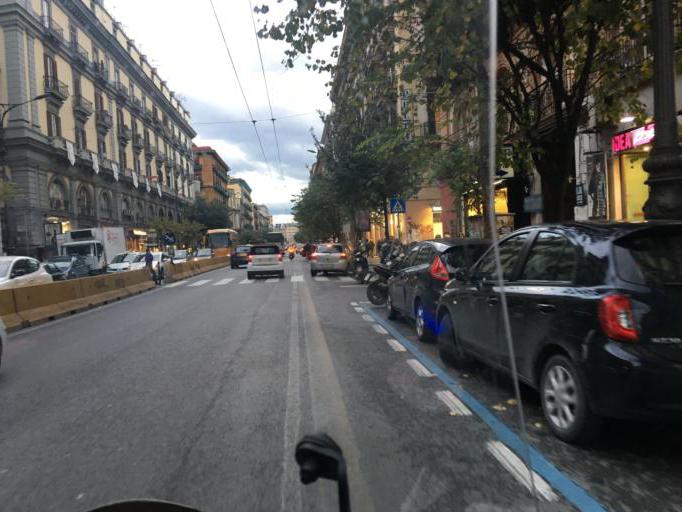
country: IT
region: Campania
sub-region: Provincia di Napoli
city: Napoli
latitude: 40.8483
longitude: 14.2628
